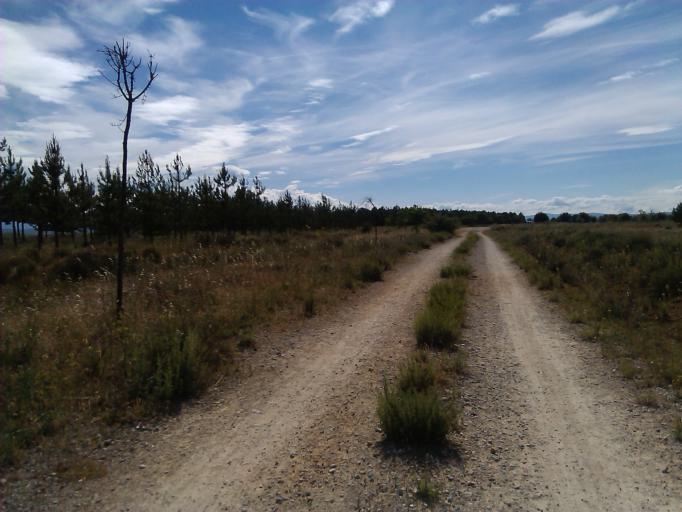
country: ES
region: Castille and Leon
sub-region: Provincia de Leon
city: San Justo de la Vega
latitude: 42.4533
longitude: -5.9934
